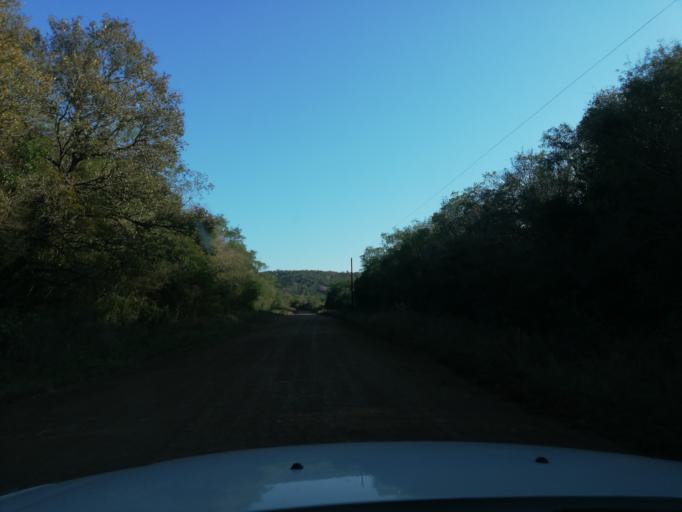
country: AR
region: Misiones
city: Cerro Cora
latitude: -27.6052
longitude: -55.7025
